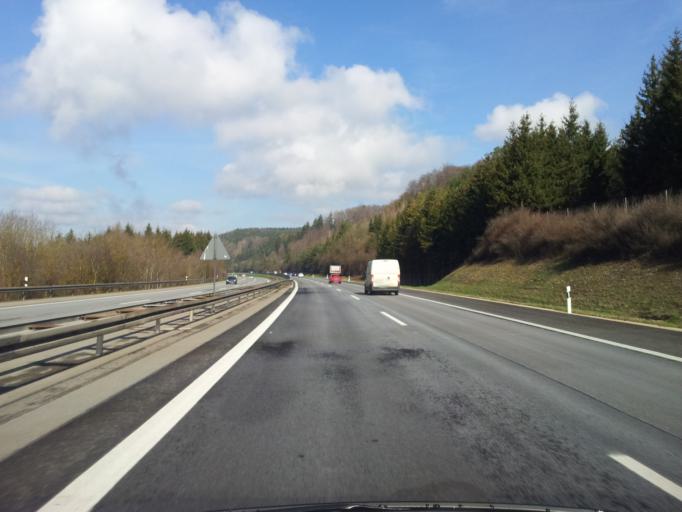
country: DE
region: Baden-Wuerttemberg
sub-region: Freiburg Region
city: Immendingen
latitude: 47.9027
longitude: 8.7002
